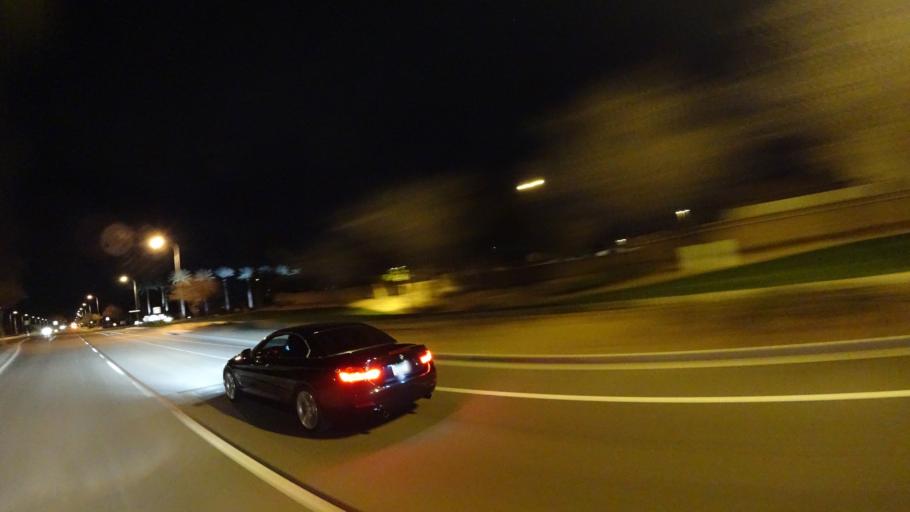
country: US
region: Arizona
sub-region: Maricopa County
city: Chandler
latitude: 33.2479
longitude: -111.8210
